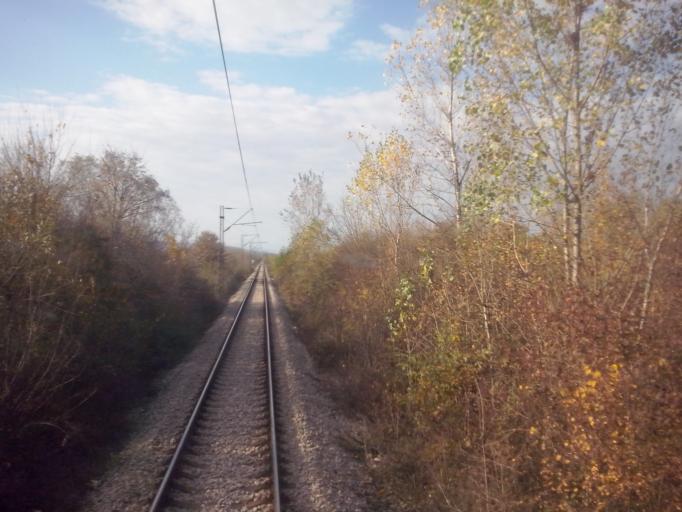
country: RS
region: Central Serbia
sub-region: Belgrade
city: Lazarevac
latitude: 44.4073
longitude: 20.2626
